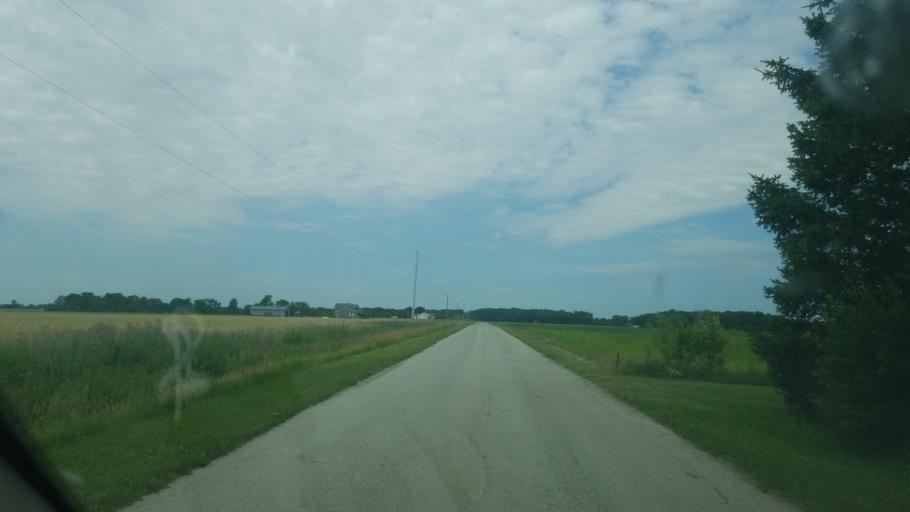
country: US
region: Ohio
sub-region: Wood County
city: North Baltimore
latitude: 41.2328
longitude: -83.6034
